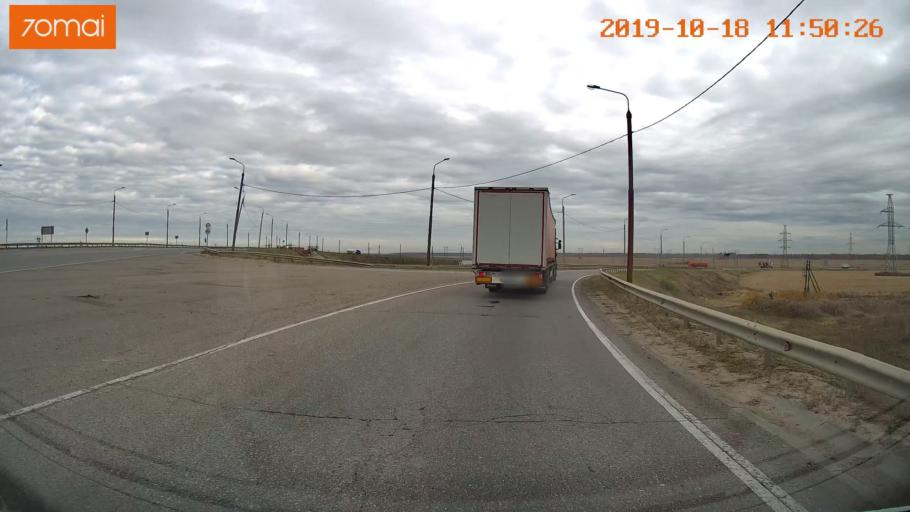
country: RU
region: Rjazan
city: Mikhaylov
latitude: 54.2606
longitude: 39.0030
